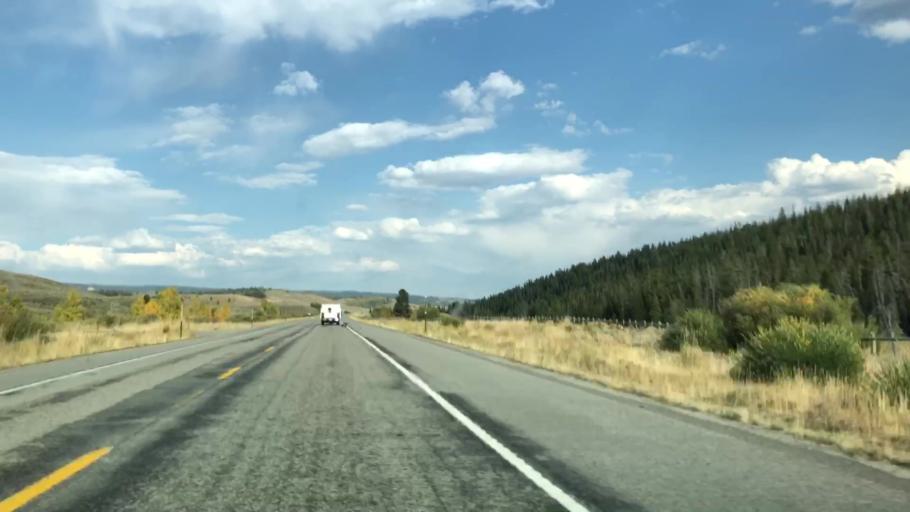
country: US
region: Wyoming
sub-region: Teton County
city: Hoback
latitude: 43.1549
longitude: -110.3251
